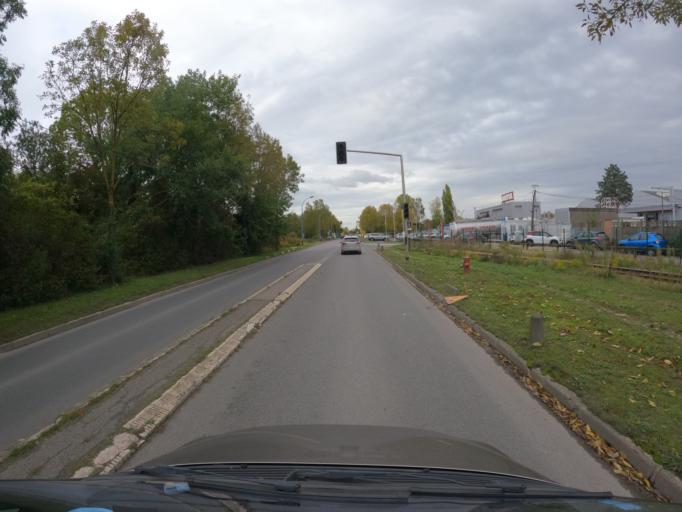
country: FR
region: Ile-de-France
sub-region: Departement de Seine-et-Marne
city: Brou-sur-Chantereine
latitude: 48.8693
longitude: 2.6178
